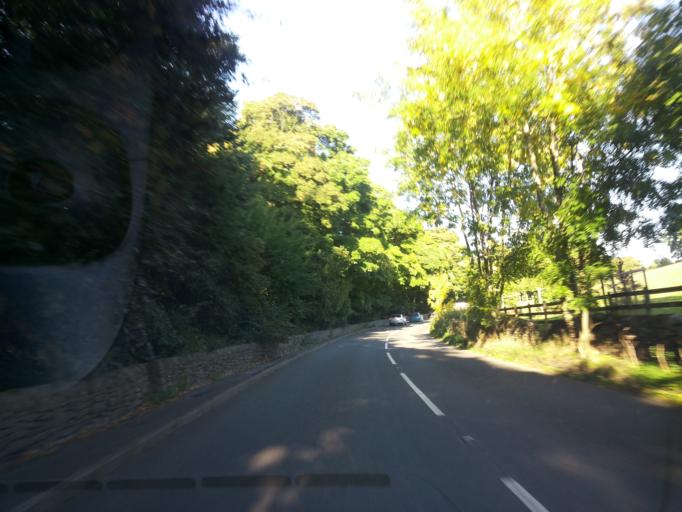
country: GB
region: England
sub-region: Derbyshire
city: Bakewell
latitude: 53.2340
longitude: -1.6983
